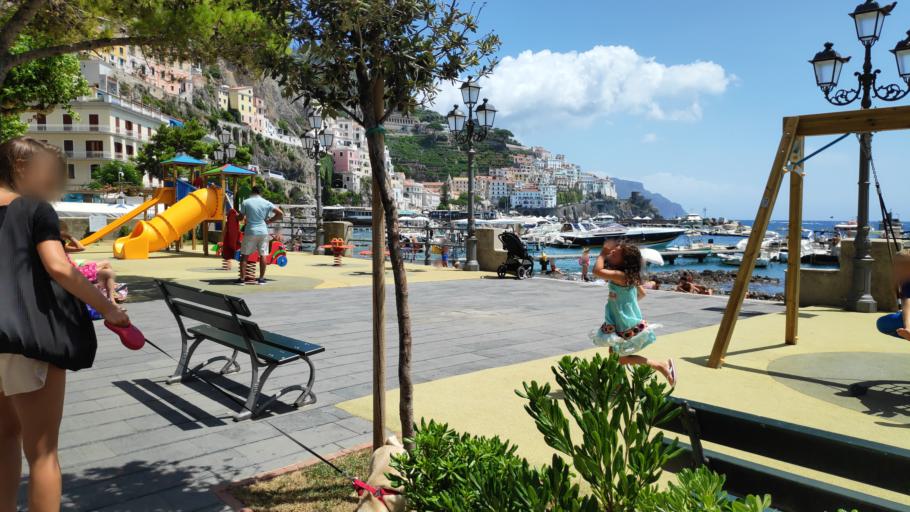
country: IT
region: Campania
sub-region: Provincia di Salerno
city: Amalfi
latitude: 40.6324
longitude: 14.5979
